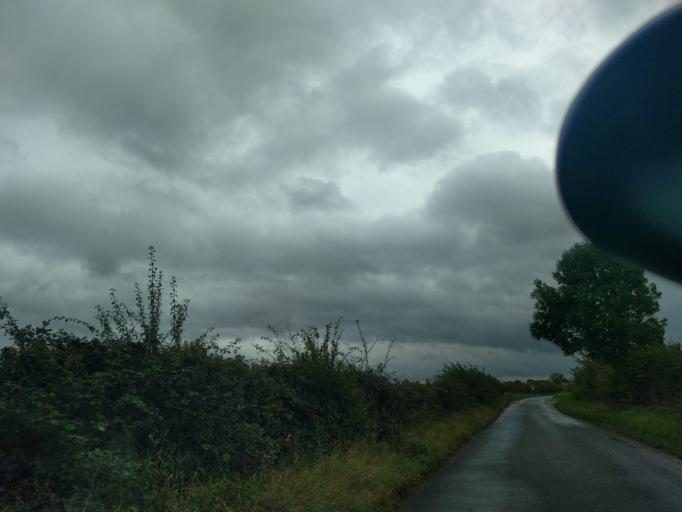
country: GB
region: England
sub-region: North Yorkshire
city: Bedale
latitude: 54.3362
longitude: -1.5775
